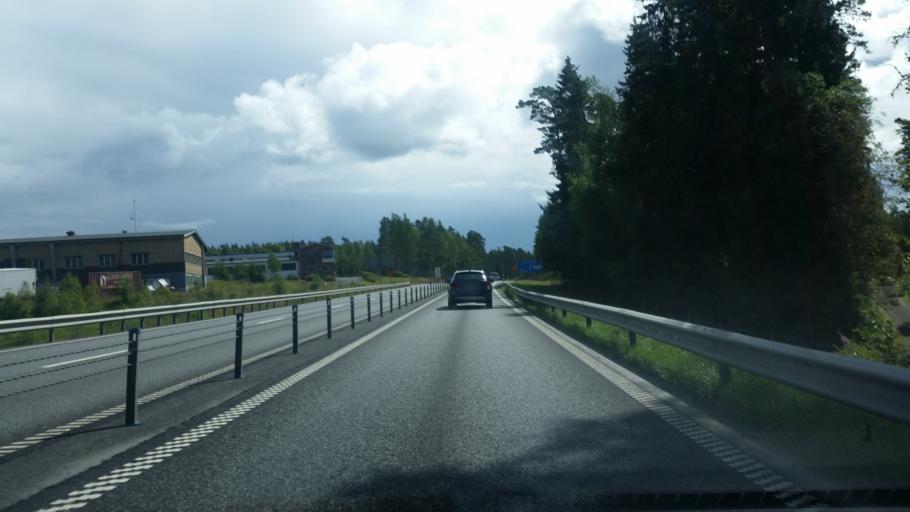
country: SE
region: Joenkoeping
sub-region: Mullsjo Kommun
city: Mullsjoe
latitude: 57.7655
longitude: 13.8230
